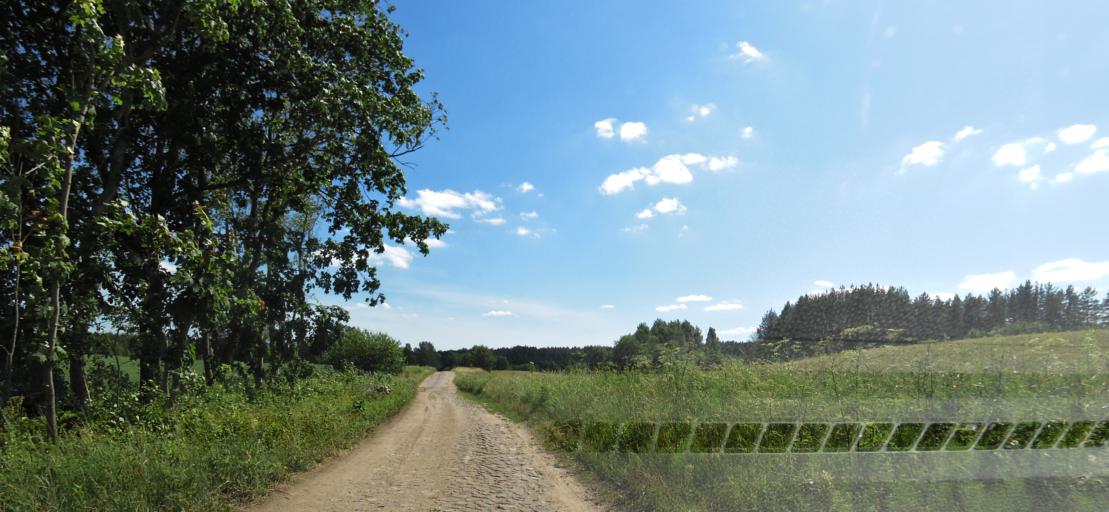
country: LT
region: Vilnius County
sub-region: Vilnius
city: Fabijoniskes
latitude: 54.8346
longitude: 25.3243
